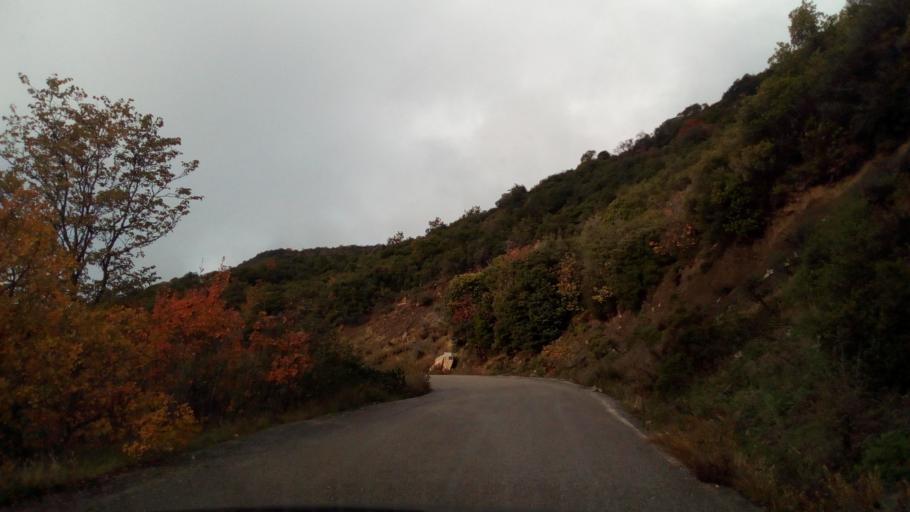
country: GR
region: West Greece
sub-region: Nomos Aitolias kai Akarnanias
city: Nafpaktos
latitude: 38.5206
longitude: 21.9758
